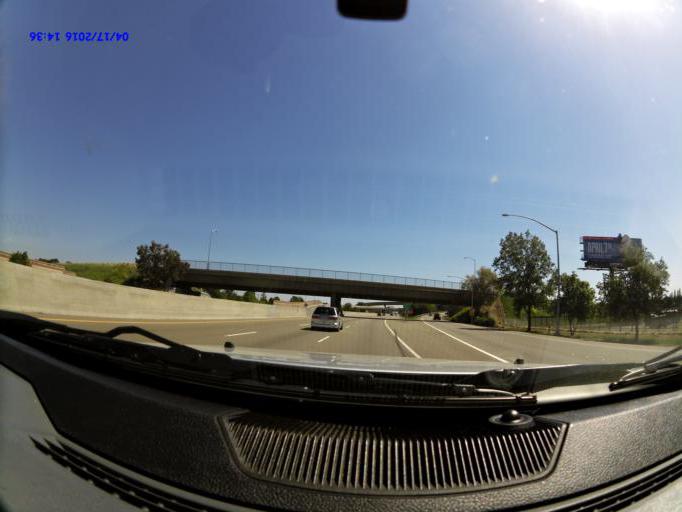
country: US
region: California
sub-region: San Joaquin County
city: Garden Acres
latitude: 37.9654
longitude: -121.2437
